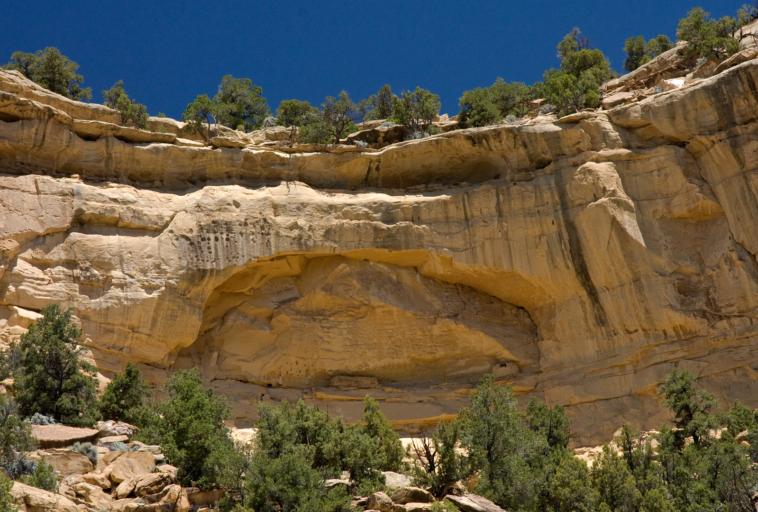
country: US
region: Utah
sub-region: Wayne County
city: Loa
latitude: 37.7420
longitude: -111.7220
